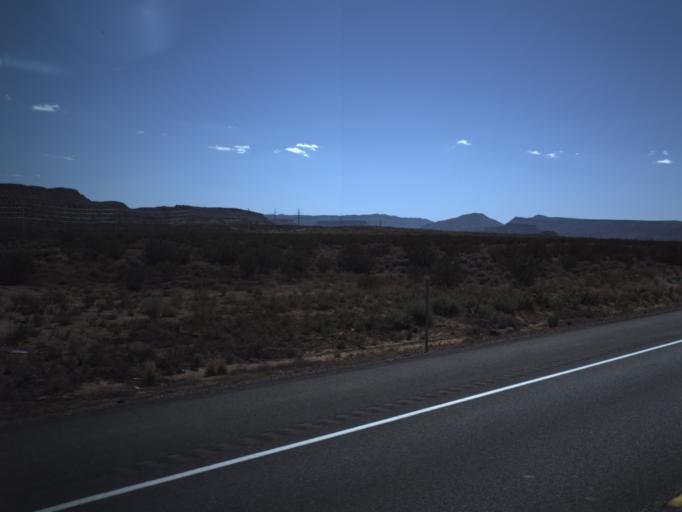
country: US
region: Utah
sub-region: Washington County
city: Washington
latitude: 37.0398
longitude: -113.4853
